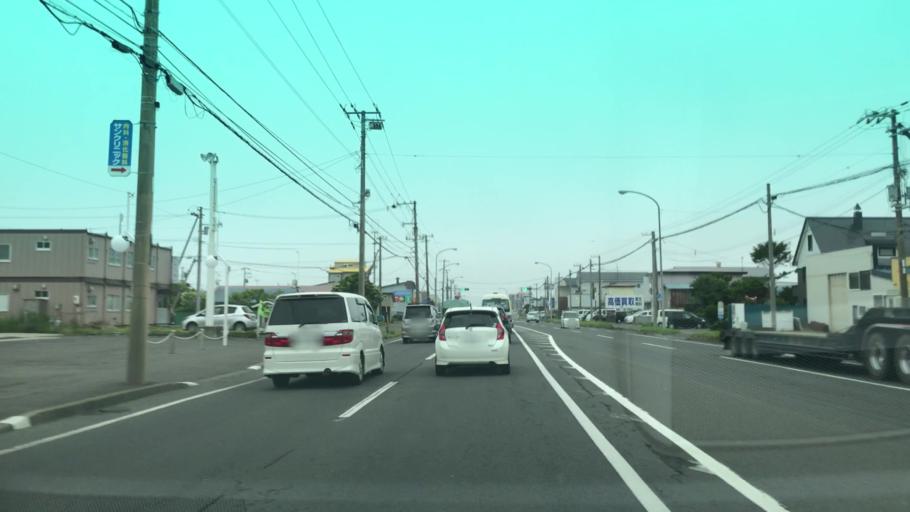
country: JP
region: Hokkaido
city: Muroran
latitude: 42.3783
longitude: 141.0710
